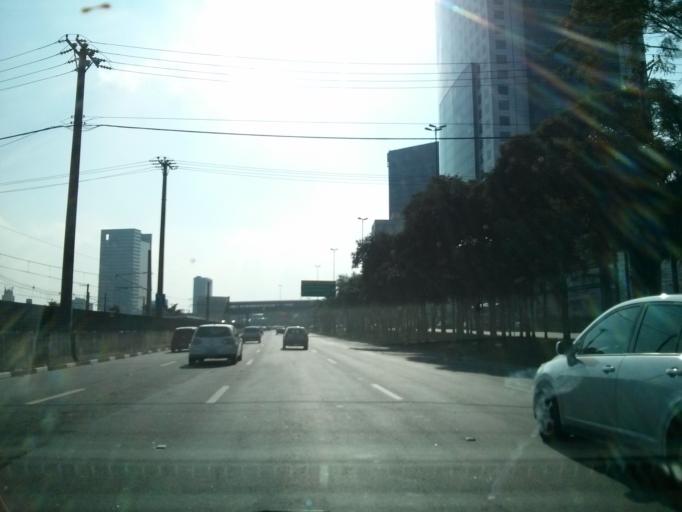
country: BR
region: Sao Paulo
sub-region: Sao Paulo
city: Sao Paulo
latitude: -23.5749
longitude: -46.6970
